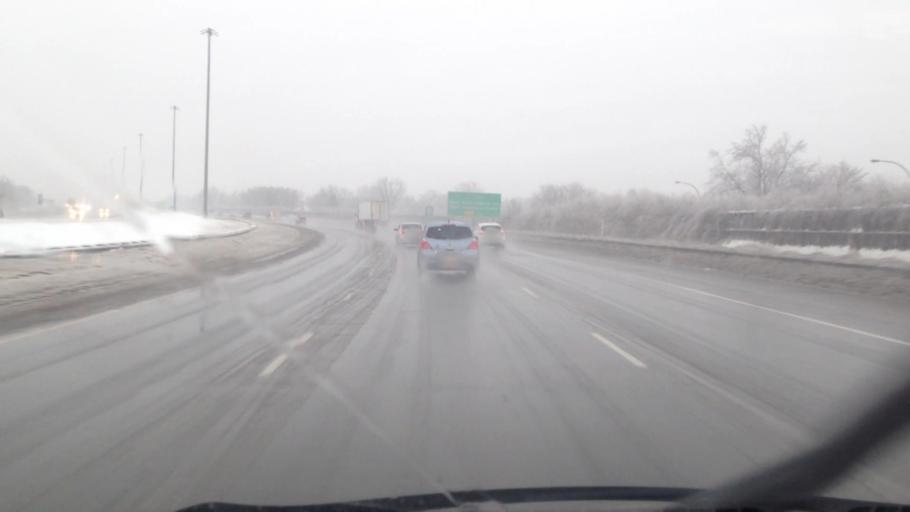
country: CA
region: Quebec
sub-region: Laurentides
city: Boisbriand
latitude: 45.5921
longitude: -73.8018
